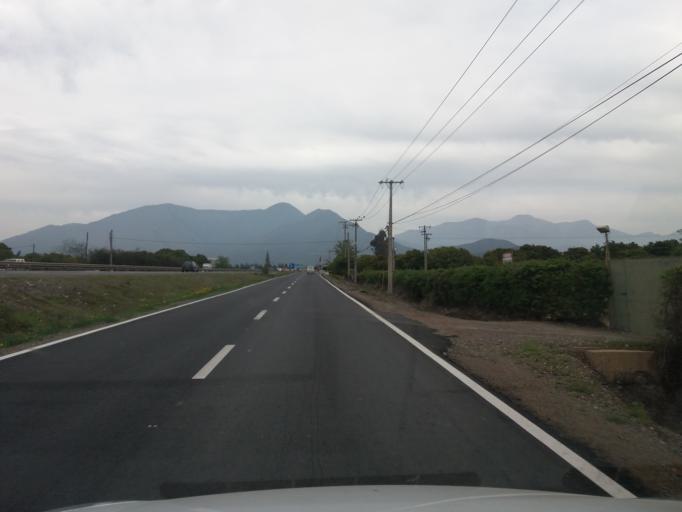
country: CL
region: Valparaiso
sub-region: Provincia de Quillota
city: Hacienda La Calera
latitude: -32.8372
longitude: -71.1168
